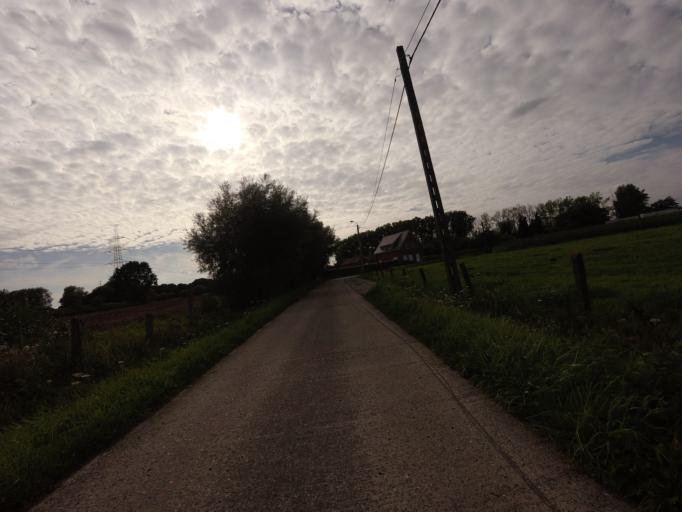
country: BE
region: Flanders
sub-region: Provincie Vlaams-Brabant
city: Londerzeel
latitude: 51.0264
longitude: 4.3267
